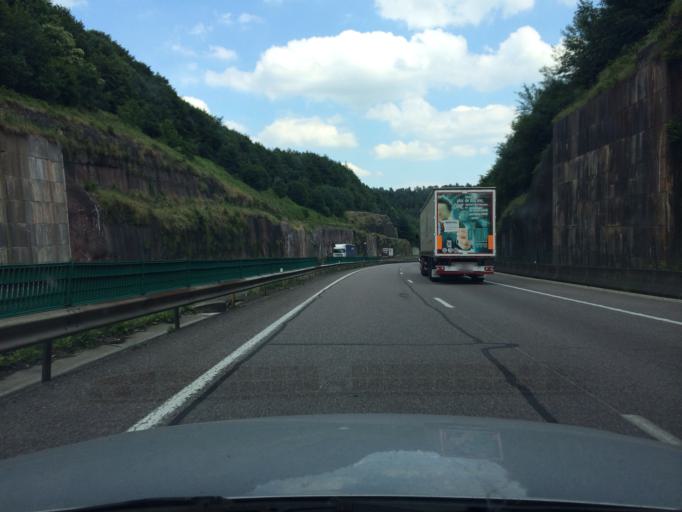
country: FR
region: Alsace
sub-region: Departement du Bas-Rhin
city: Saverne
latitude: 48.7729
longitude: 7.3279
